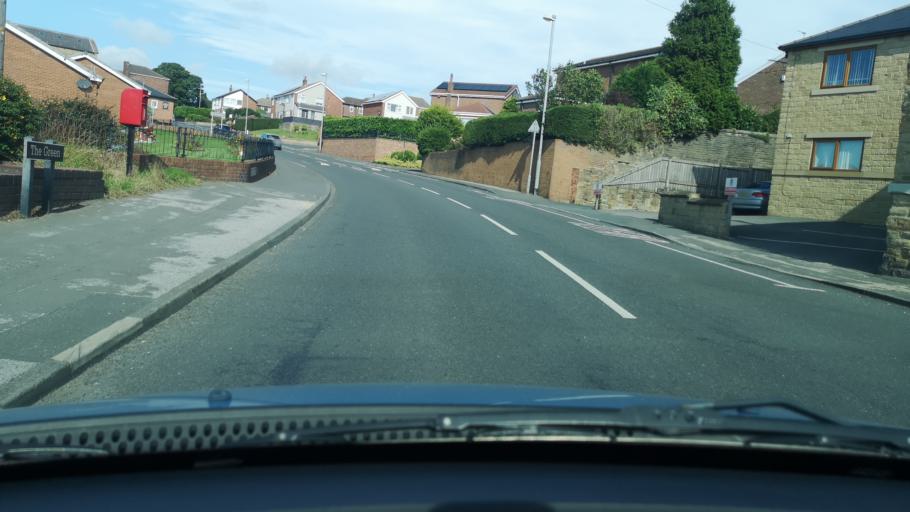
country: GB
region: England
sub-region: City and Borough of Wakefield
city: Ossett
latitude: 53.6758
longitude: -1.5788
